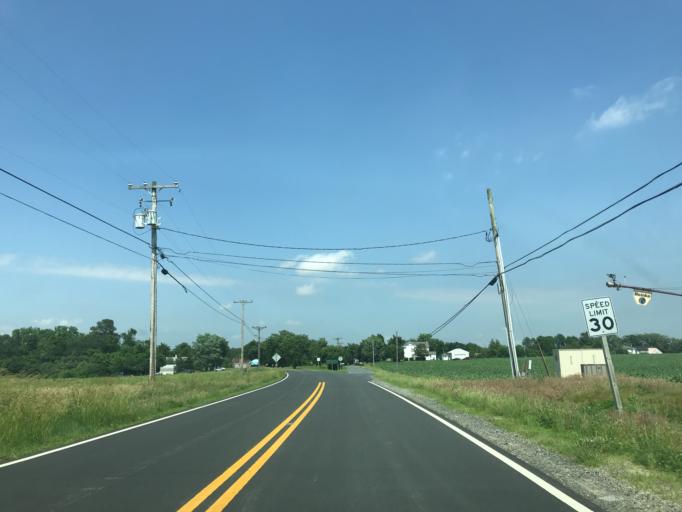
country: US
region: Maryland
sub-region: Dorchester County
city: Hurlock
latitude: 38.5741
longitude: -75.7982
